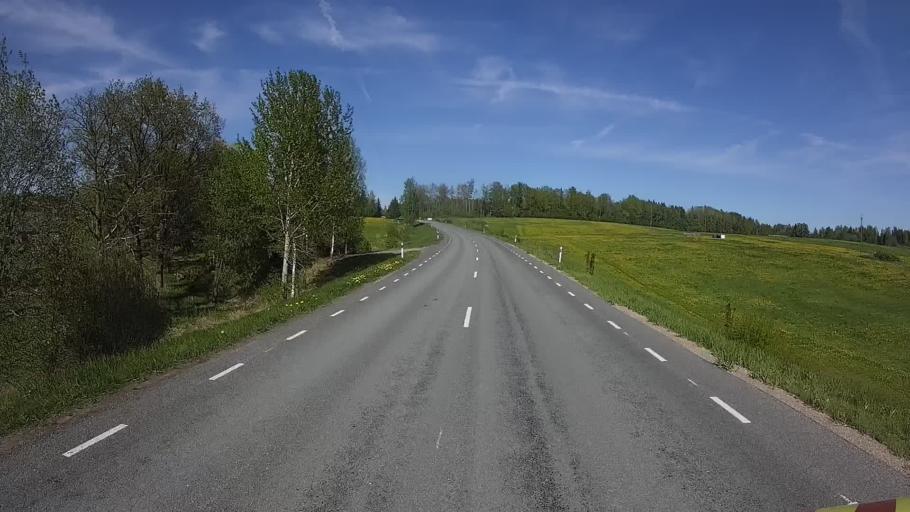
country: EE
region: Vorumaa
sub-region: Antsla vald
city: Vana-Antsla
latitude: 57.9529
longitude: 26.4419
